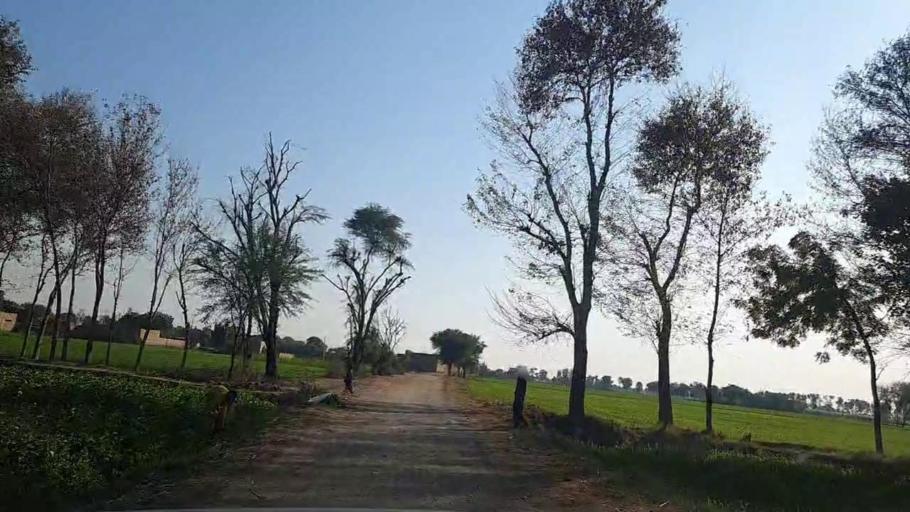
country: PK
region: Sindh
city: Sakrand
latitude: 26.3135
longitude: 68.1818
